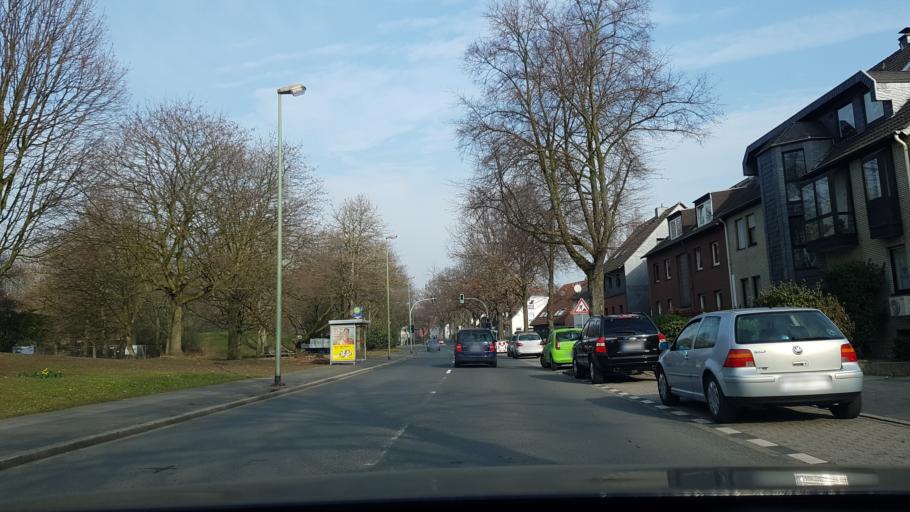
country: DE
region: North Rhine-Westphalia
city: Meiderich
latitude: 51.4997
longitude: 6.7978
